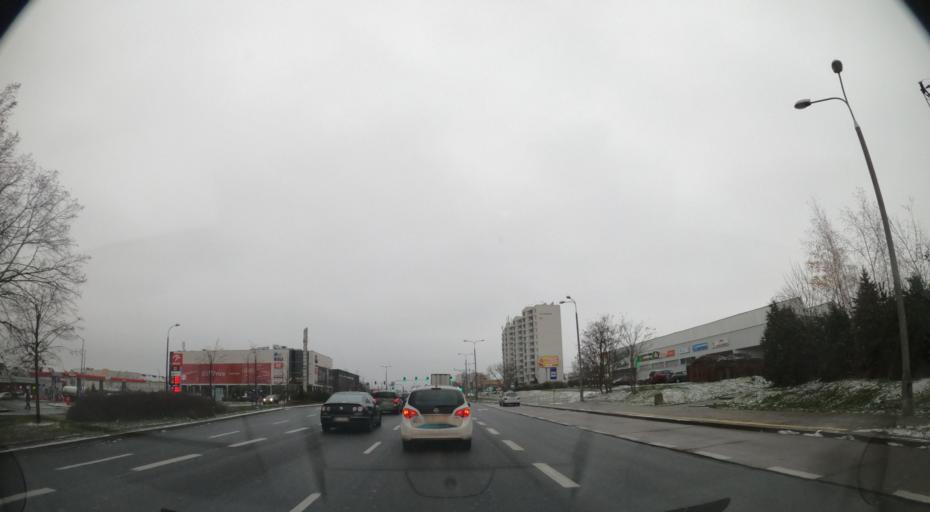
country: PL
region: Masovian Voivodeship
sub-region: Plock
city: Plock
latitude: 52.5348
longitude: 19.7618
